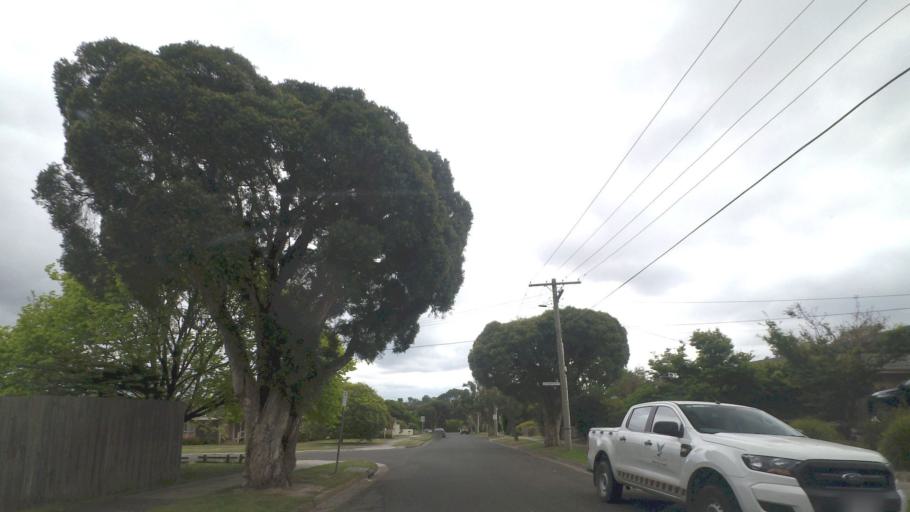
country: AU
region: Victoria
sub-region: Knox
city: Bayswater
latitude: -37.8538
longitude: 145.2616
